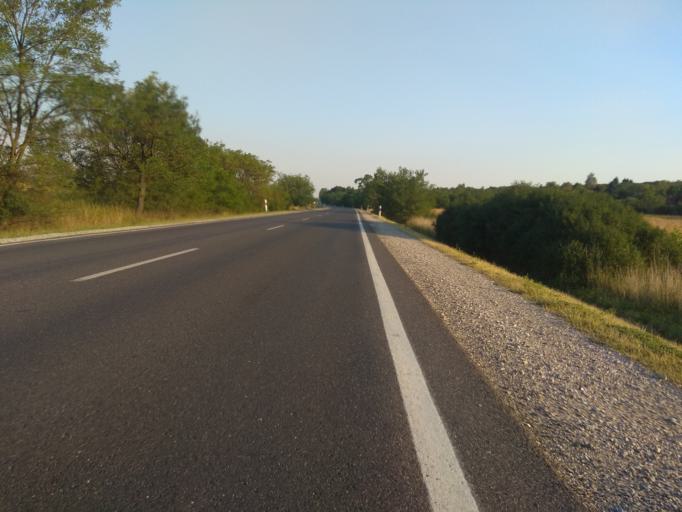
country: HU
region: Borsod-Abauj-Zemplen
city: Nyekladhaza
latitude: 47.9711
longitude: 20.8310
